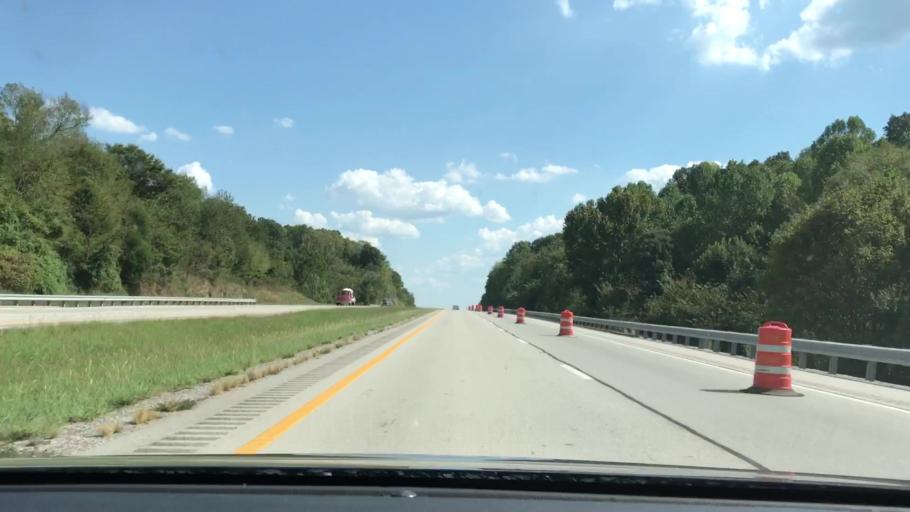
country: US
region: Kentucky
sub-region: Butler County
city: Morgantown
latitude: 37.2286
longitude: -86.7240
